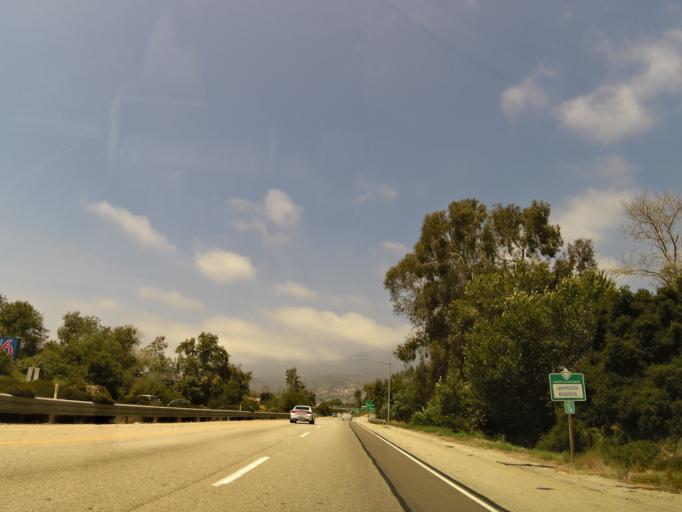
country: US
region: California
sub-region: Santa Barbara County
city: Carpinteria
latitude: 34.3934
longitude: -119.5092
